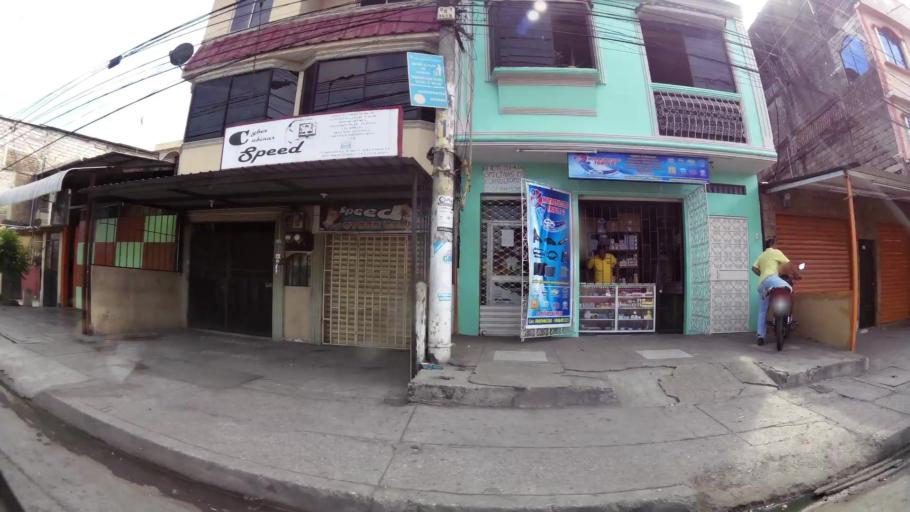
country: EC
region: Guayas
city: Guayaquil
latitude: -2.2595
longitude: -79.8846
